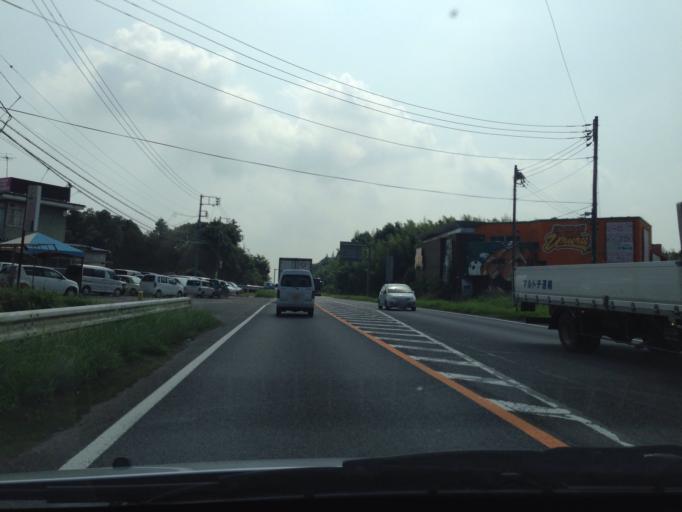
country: JP
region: Ibaraki
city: Ami
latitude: 36.0217
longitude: 140.2445
